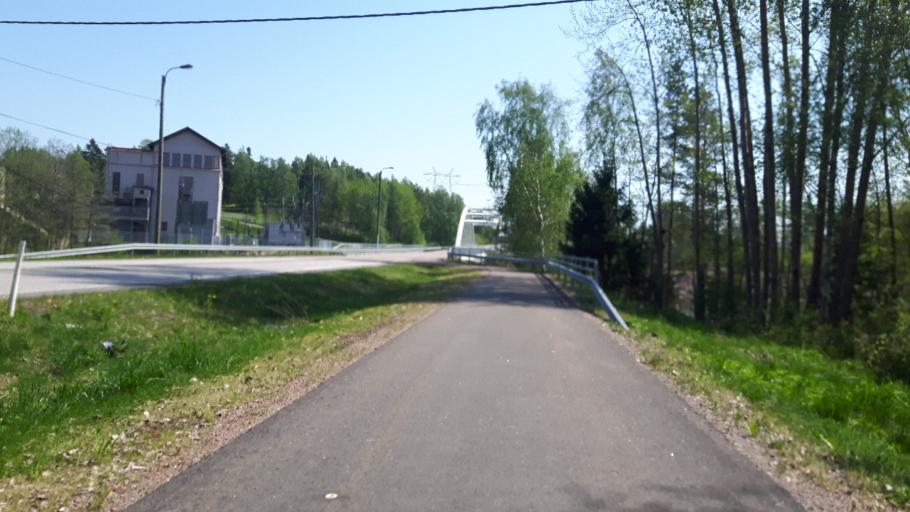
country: FI
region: Uusimaa
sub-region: Loviisa
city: Ruotsinpyhtaeae
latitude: 60.4938
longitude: 26.4476
